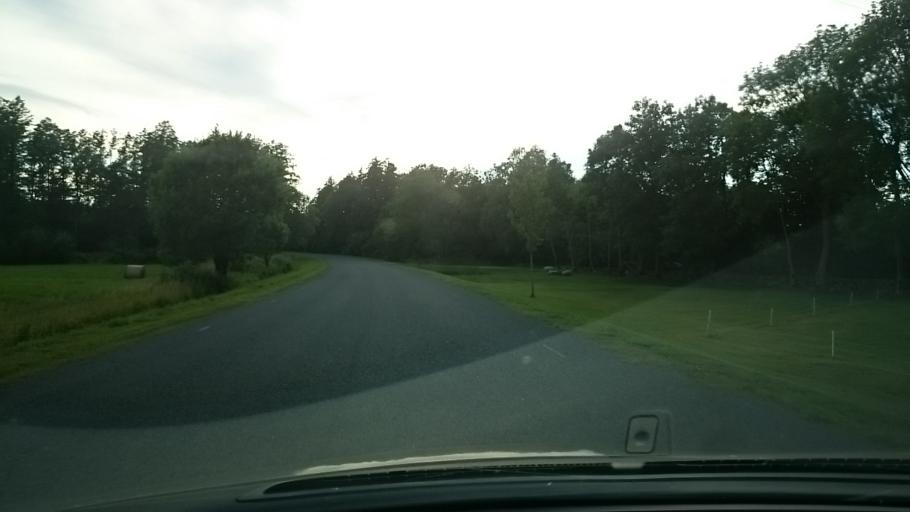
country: EE
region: Saare
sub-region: Kuressaare linn
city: Kuressaare
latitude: 58.4194
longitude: 22.1500
